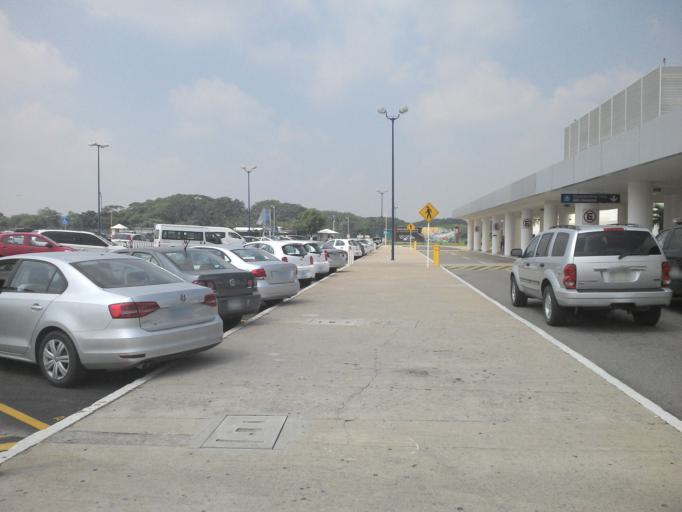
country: MX
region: Tabasco
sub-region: Centro
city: El Bajio
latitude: 17.9925
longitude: -92.8186
